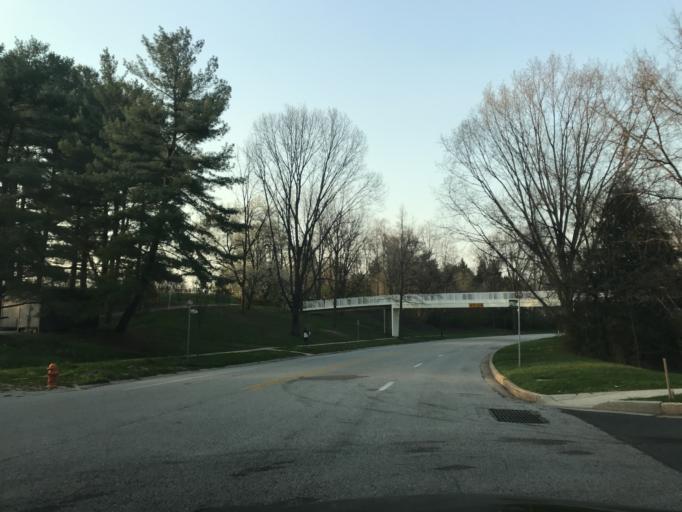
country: US
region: Maryland
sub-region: Howard County
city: Columbia
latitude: 39.2275
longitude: -76.8561
